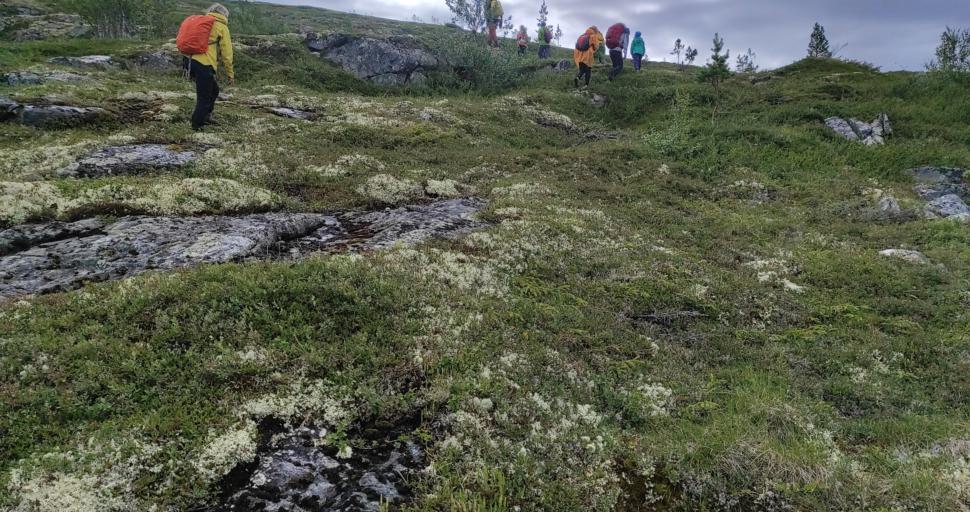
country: RU
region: Murmansk
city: Afrikanda
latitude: 67.0506
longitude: 32.9205
